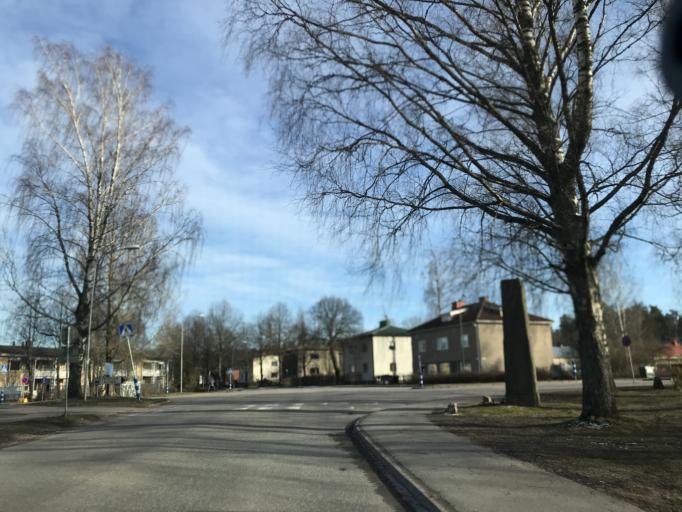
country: FI
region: Uusimaa
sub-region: Raaseporin
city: Karis
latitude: 60.0766
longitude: 23.6801
